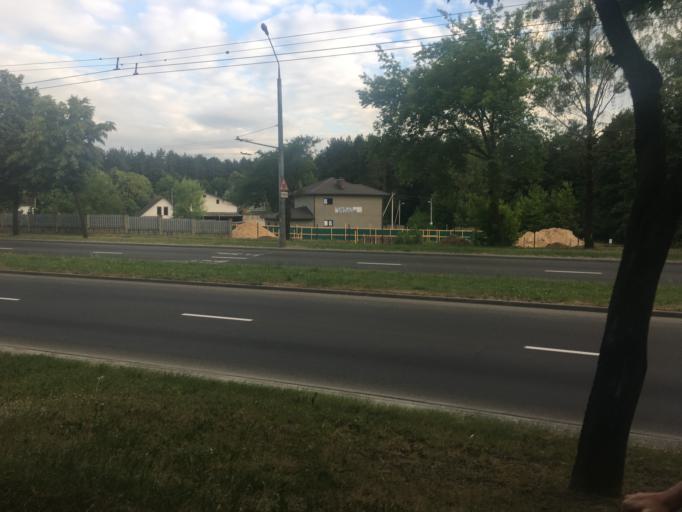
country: BY
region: Grodnenskaya
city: Hrodna
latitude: 53.6853
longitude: 23.8020
